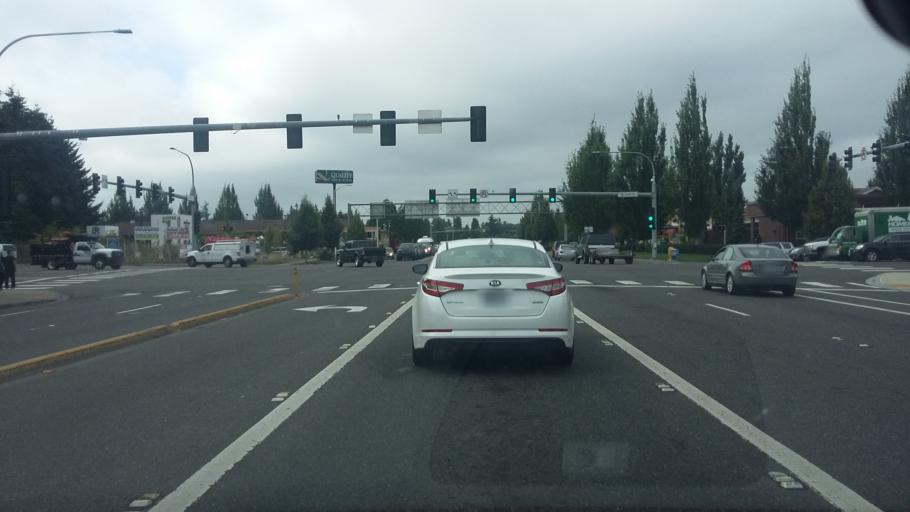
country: US
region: Washington
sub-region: Clark County
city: Salmon Creek
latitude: 45.7187
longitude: -122.6514
